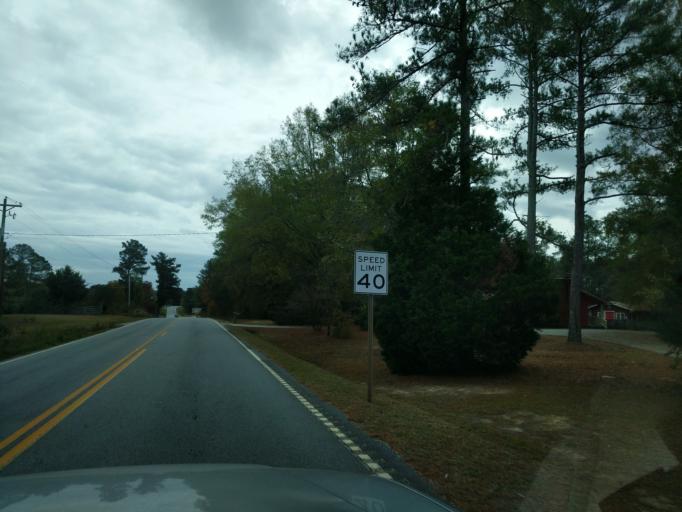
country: US
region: South Carolina
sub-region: Saluda County
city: Saluda
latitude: 34.0177
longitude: -81.7852
